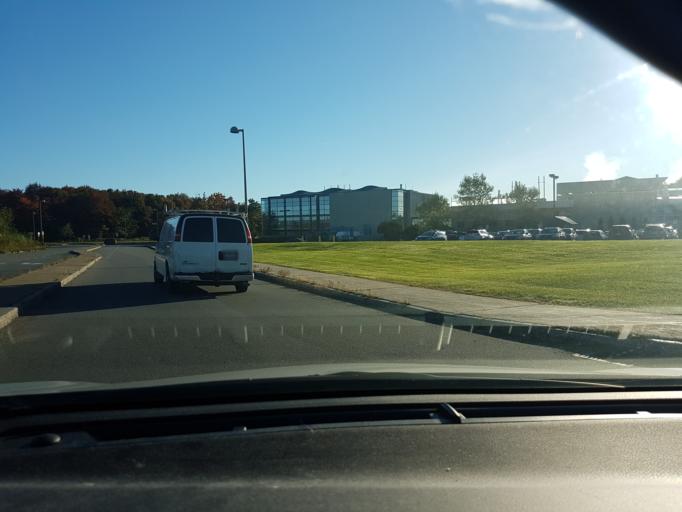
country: CA
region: Quebec
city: L'Ancienne-Lorette
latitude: 46.7958
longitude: -71.3151
